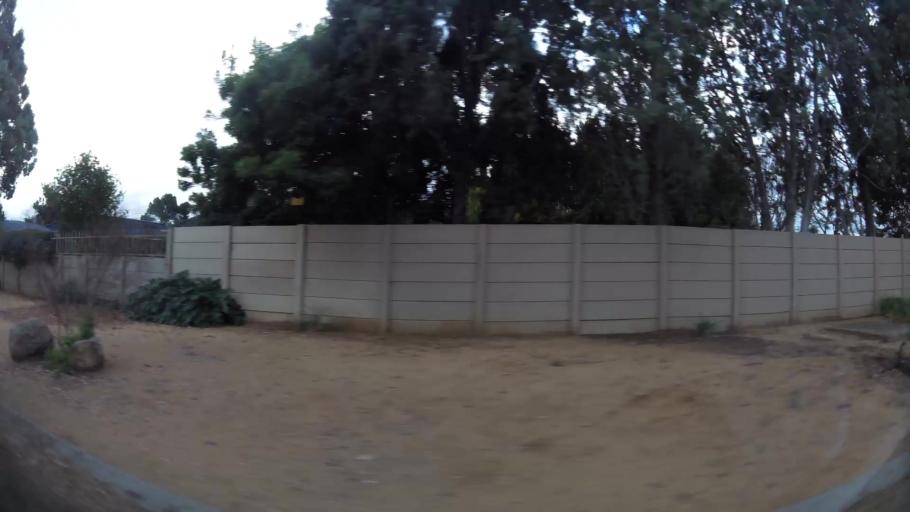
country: ZA
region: Orange Free State
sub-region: Lejweleputswa District Municipality
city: Welkom
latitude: -27.9789
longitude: 26.7303
